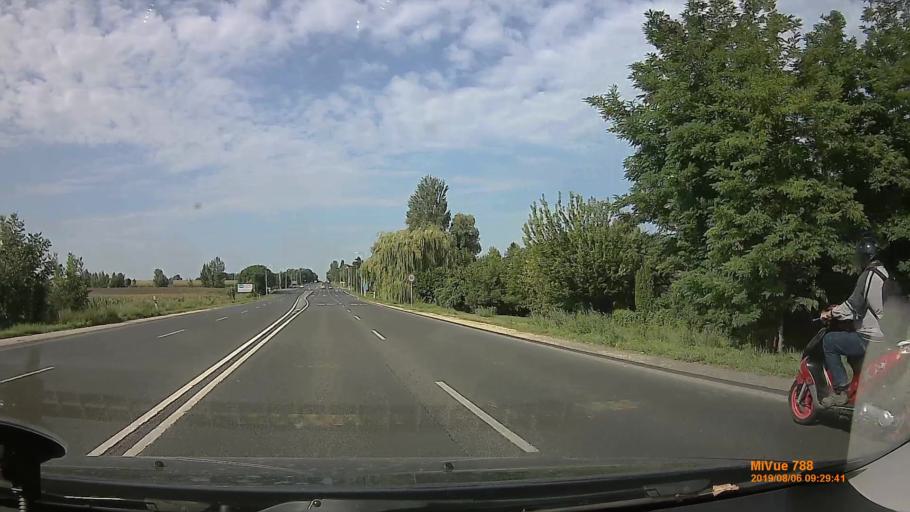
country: HU
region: Somogy
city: Balatonszarszo
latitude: 46.8351
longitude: 17.8502
